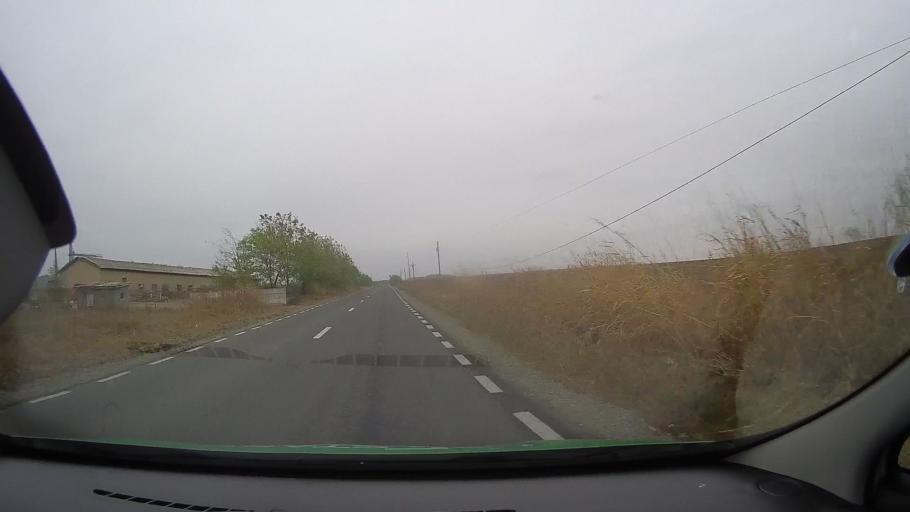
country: RO
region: Constanta
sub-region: Comuna Tortoman
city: Tortoman
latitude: 44.3632
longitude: 28.2094
